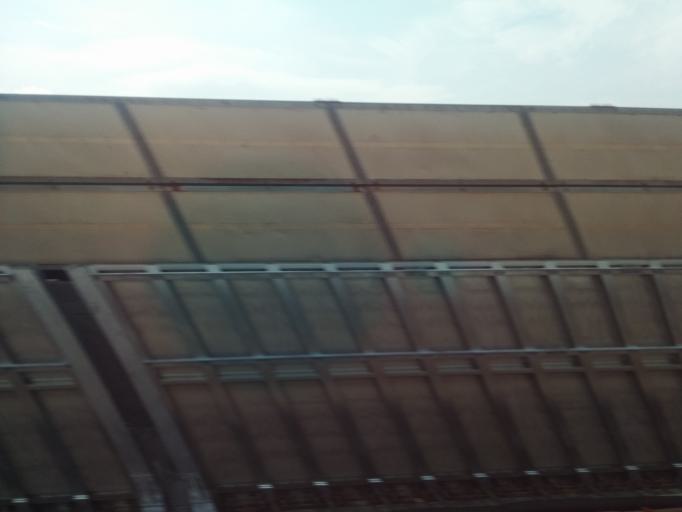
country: JP
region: Kanagawa
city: Yokohama
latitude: 35.4790
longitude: 139.5668
